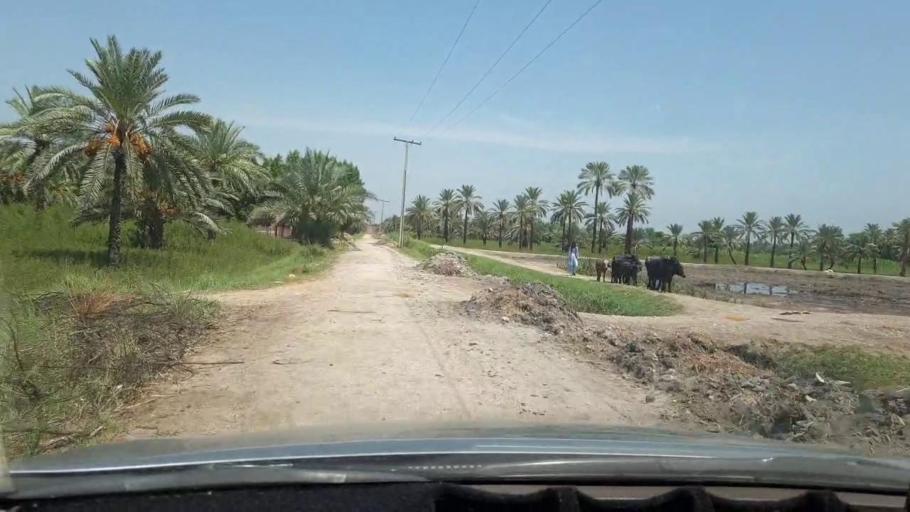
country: PK
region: Sindh
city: Khairpur
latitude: 27.4881
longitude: 68.7701
